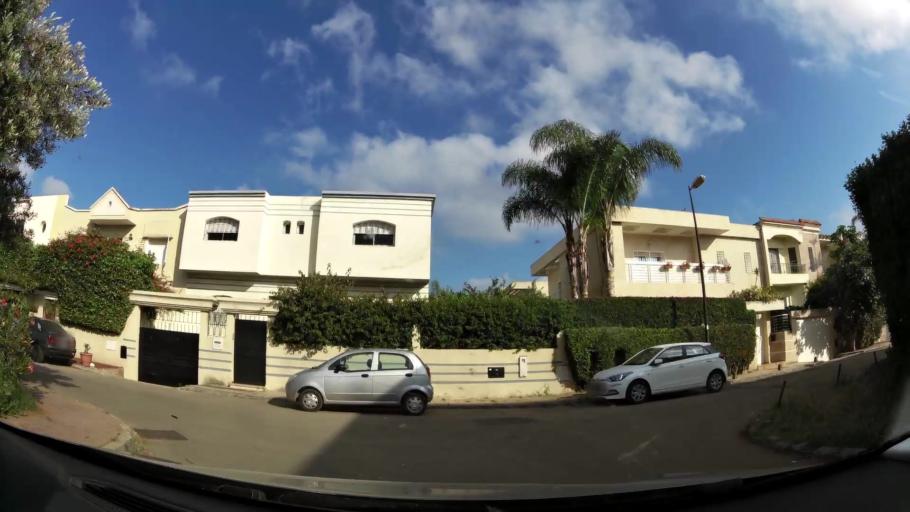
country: MA
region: Rabat-Sale-Zemmour-Zaer
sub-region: Skhirate-Temara
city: Temara
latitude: 33.9522
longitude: -6.8603
